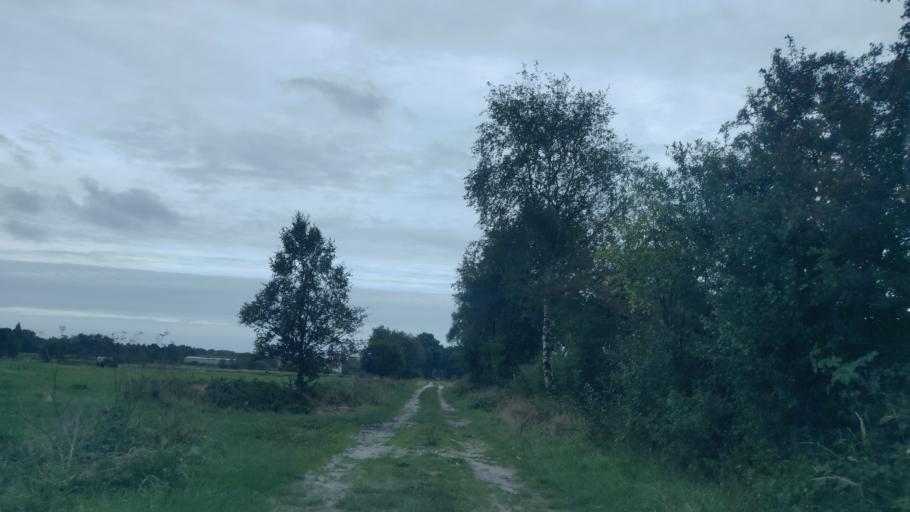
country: DE
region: Lower Saxony
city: Aurich
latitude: 53.5325
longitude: 7.4765
